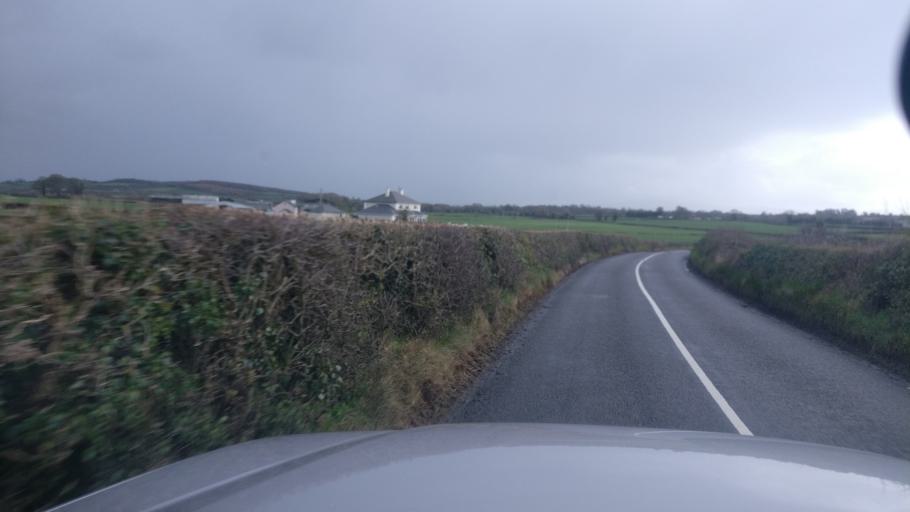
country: IE
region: Munster
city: Nenagh Bridge
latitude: 52.9652
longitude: -8.0861
